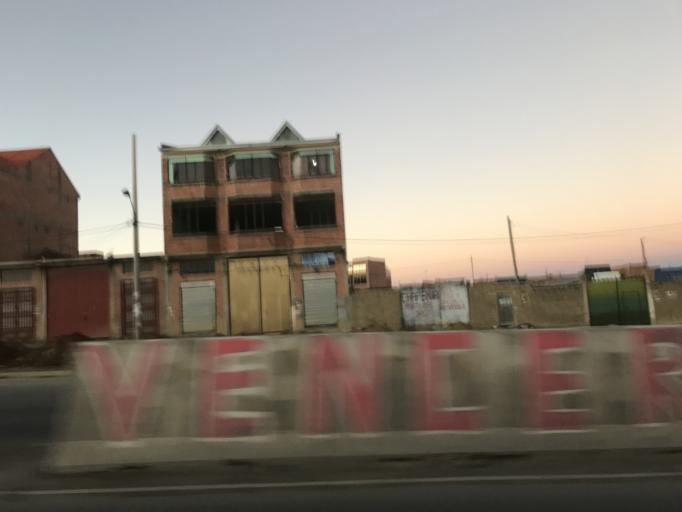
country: BO
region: La Paz
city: La Paz
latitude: -16.4772
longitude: -68.2651
